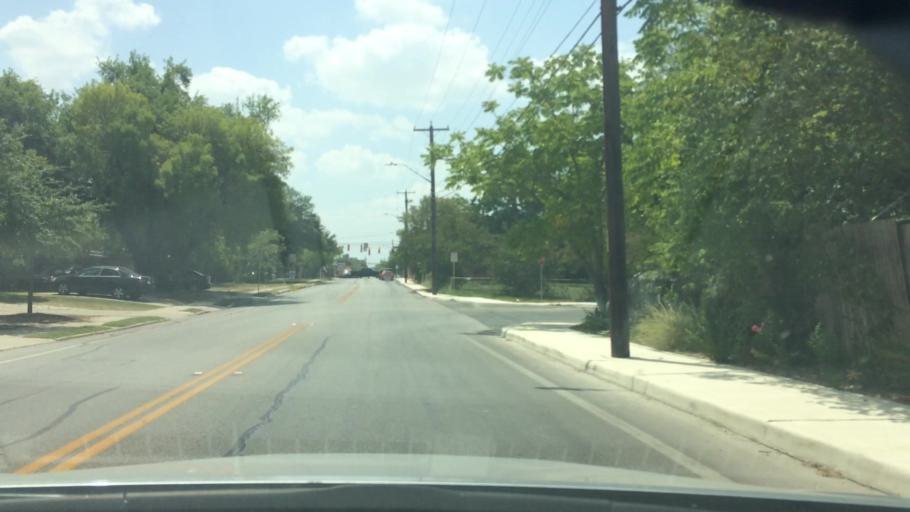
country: US
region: Texas
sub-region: Bexar County
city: Olmos Park
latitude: 29.5043
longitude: -98.4901
